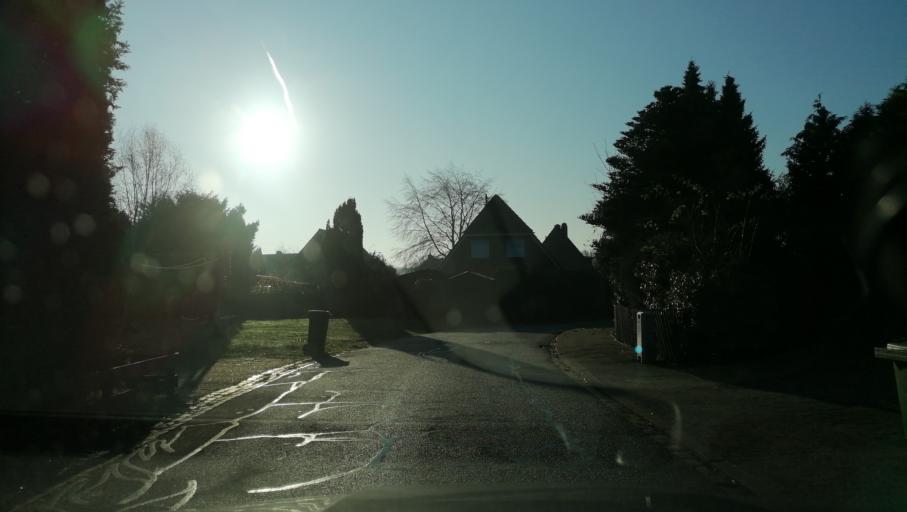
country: DE
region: Schleswig-Holstein
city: Nindorf
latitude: 54.0900
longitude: 9.0936
